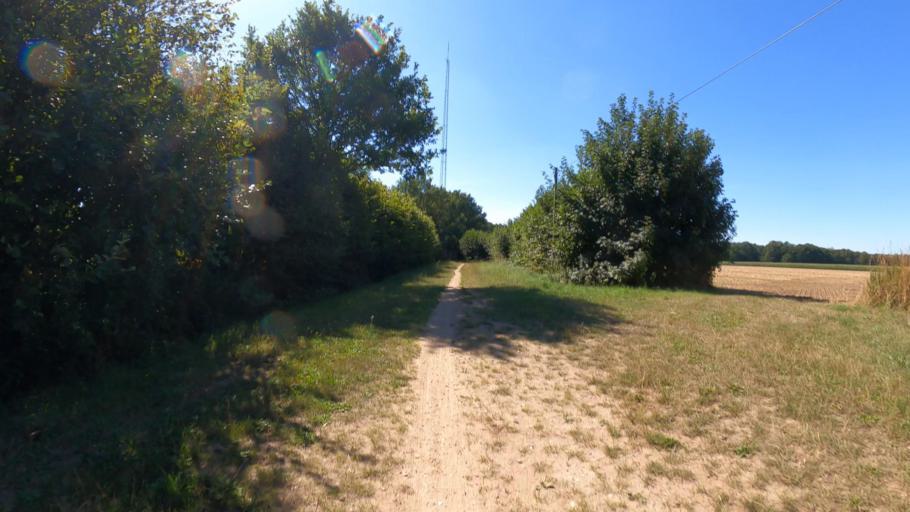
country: DE
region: Schleswig-Holstein
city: Kroppelshagen-Fahrendorf
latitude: 53.4613
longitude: 10.3498
